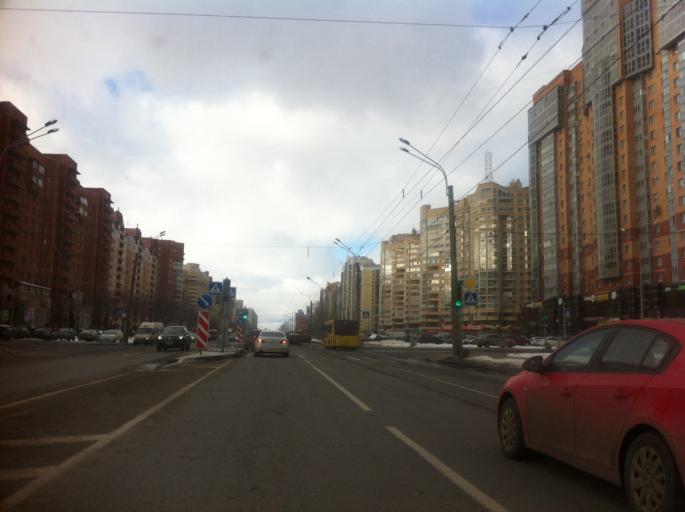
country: RU
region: St.-Petersburg
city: Uritsk
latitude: 59.8566
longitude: 30.2007
